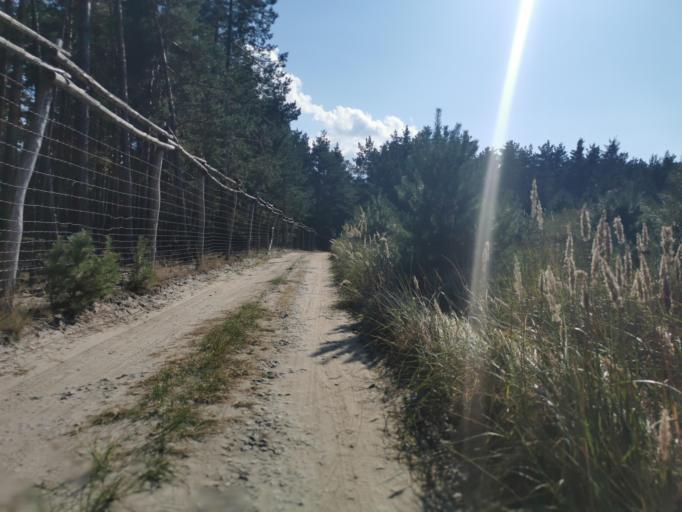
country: SK
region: Trnavsky
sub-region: Okres Senica
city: Senica
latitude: 48.6112
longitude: 17.2761
